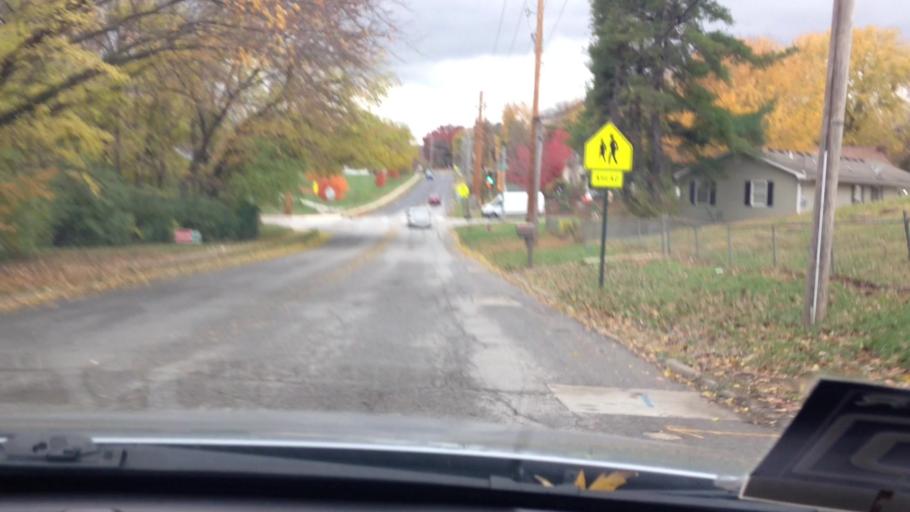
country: US
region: Kansas
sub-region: Leavenworth County
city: Leavenworth
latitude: 39.2959
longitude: -94.9127
